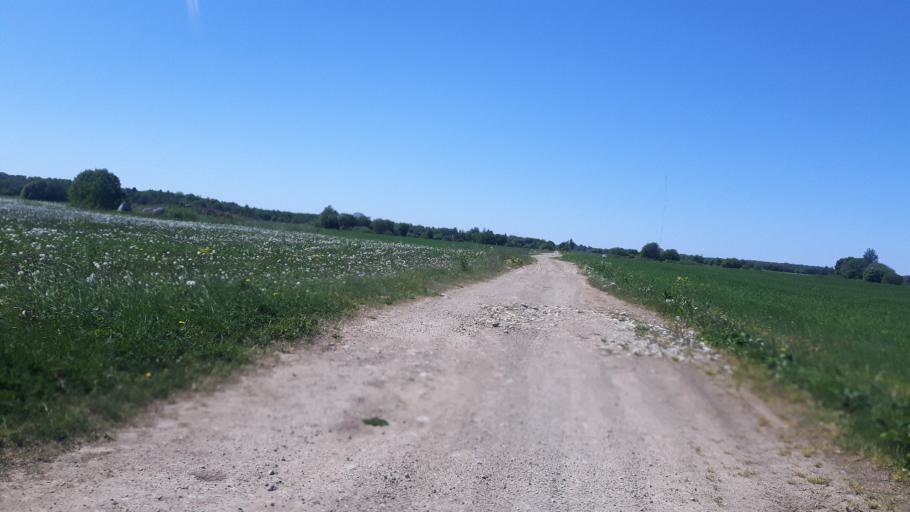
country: EE
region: Ida-Virumaa
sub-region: Toila vald
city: Voka
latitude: 59.4037
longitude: 27.6573
